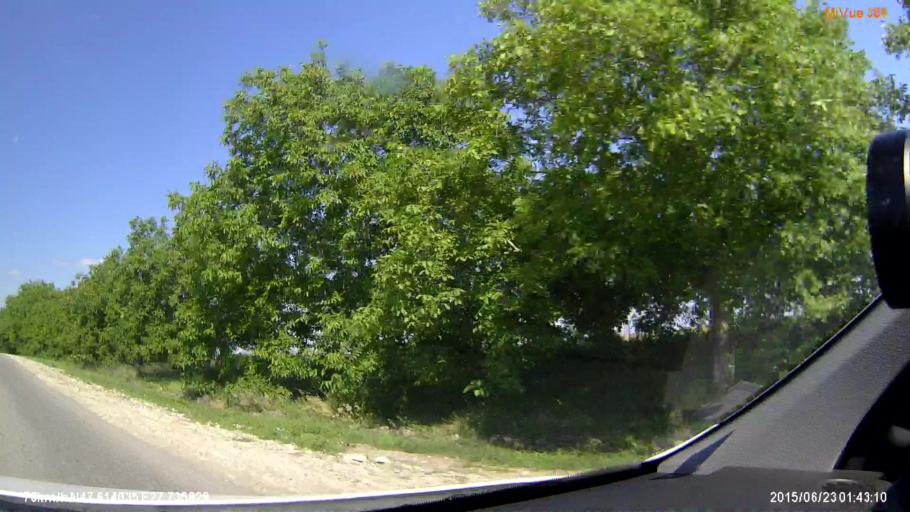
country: MD
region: Falesti
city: Falesti
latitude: 47.6139
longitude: 27.7356
